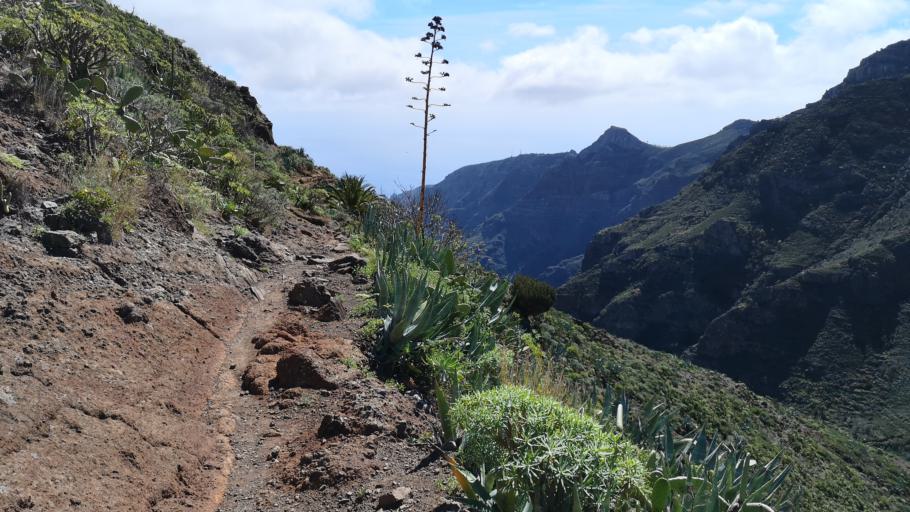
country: ES
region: Canary Islands
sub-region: Provincia de Santa Cruz de Tenerife
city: Alajero
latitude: 28.0844
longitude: -17.2334
